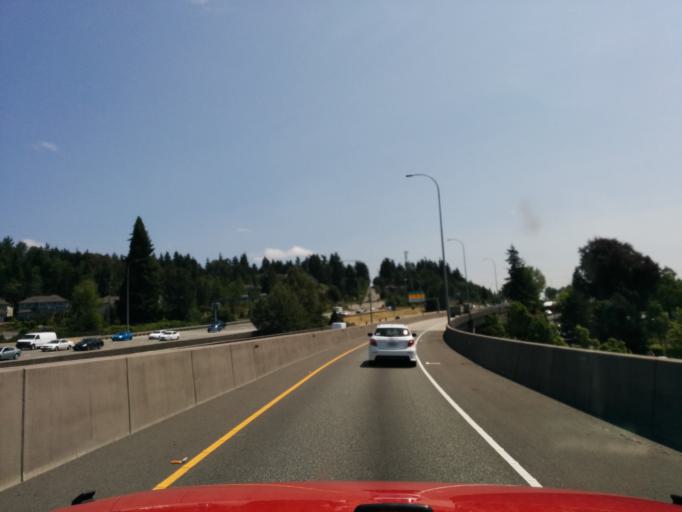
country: US
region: Washington
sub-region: King County
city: Bellevue
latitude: 47.6318
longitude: -122.1820
